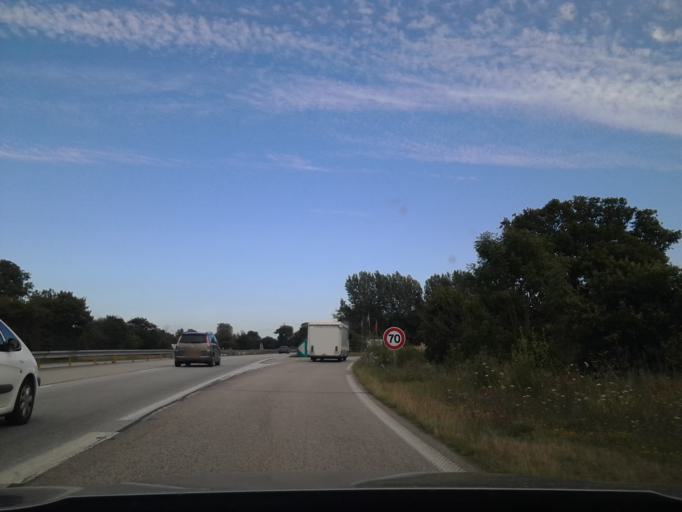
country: FR
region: Lower Normandy
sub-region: Departement de la Manche
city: Valognes
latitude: 49.5221
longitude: -1.5023
